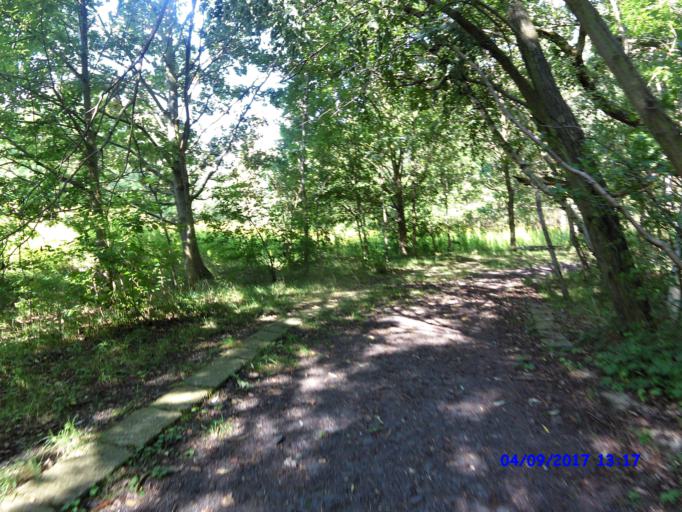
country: DE
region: Saxony
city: Taucha
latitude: 51.3522
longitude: 12.4703
